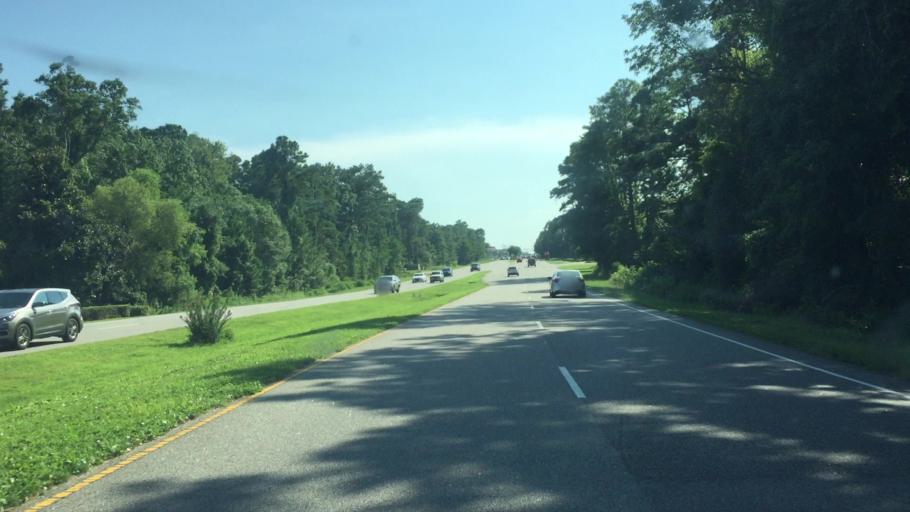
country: US
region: South Carolina
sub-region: Horry County
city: Myrtle Beach
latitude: 33.7554
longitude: -78.8088
